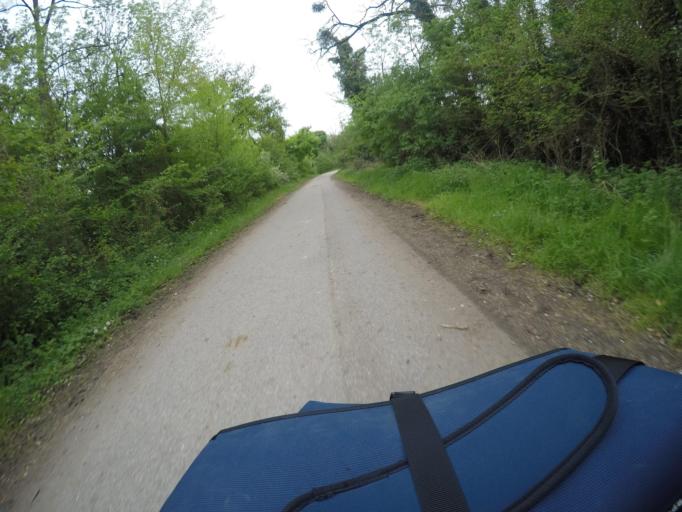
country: FR
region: Alsace
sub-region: Departement du Bas-Rhin
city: Eschau
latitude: 48.5084
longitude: 7.7379
